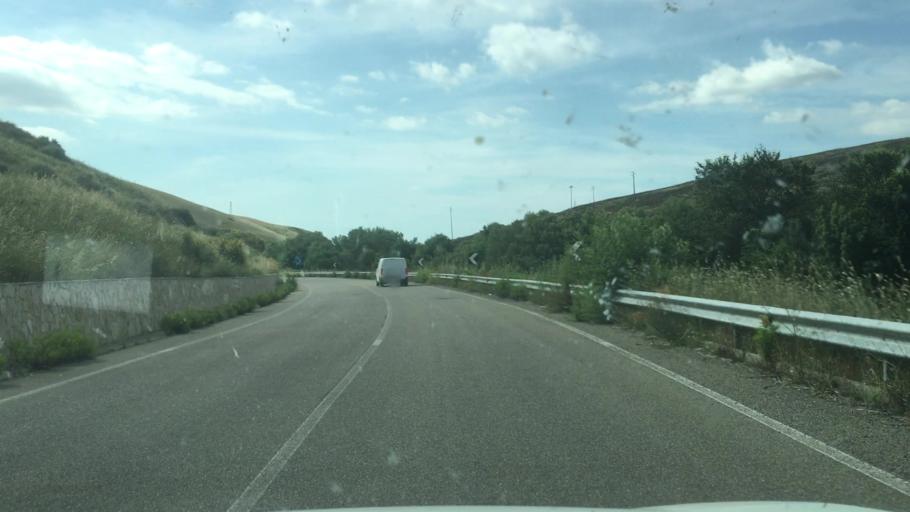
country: IT
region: Basilicate
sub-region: Provincia di Matera
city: Salandra
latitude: 40.5314
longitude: 16.2881
